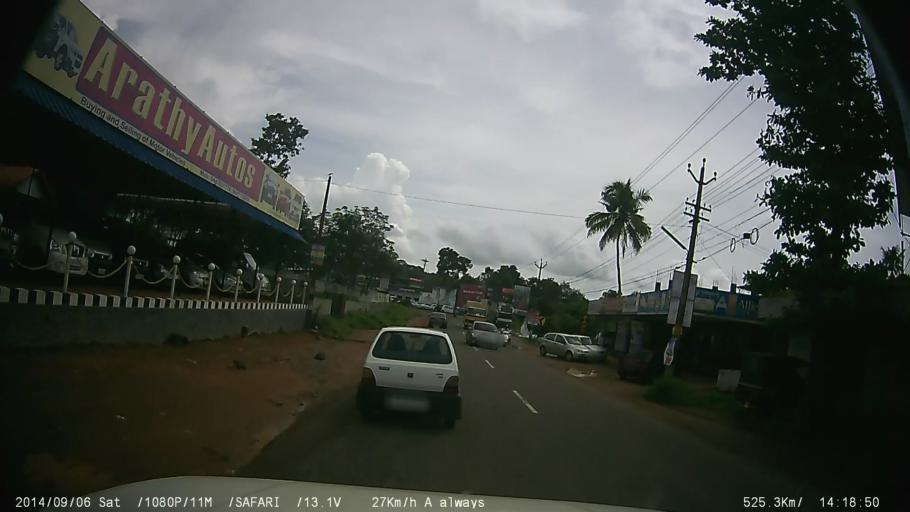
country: IN
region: Kerala
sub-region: Kottayam
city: Kottayam
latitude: 9.6610
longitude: 76.5505
